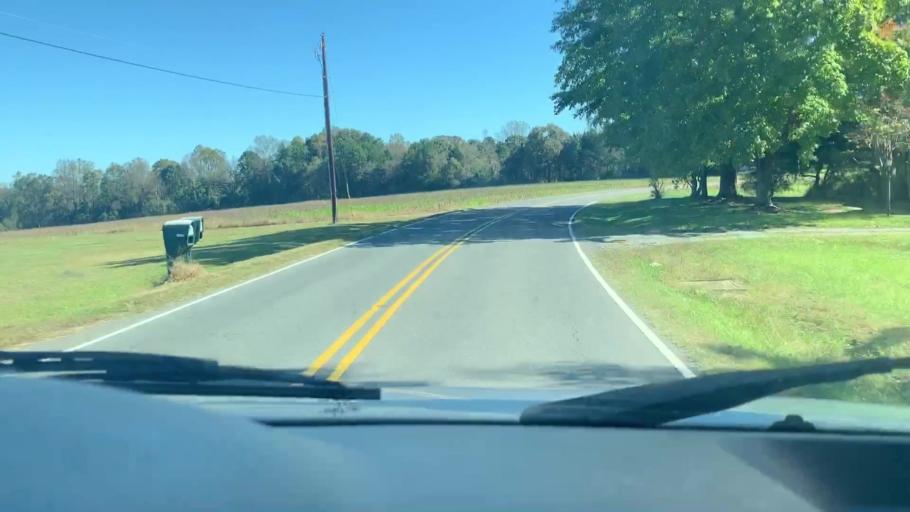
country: US
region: North Carolina
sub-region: Mecklenburg County
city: Cornelius
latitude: 35.4547
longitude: -80.8349
